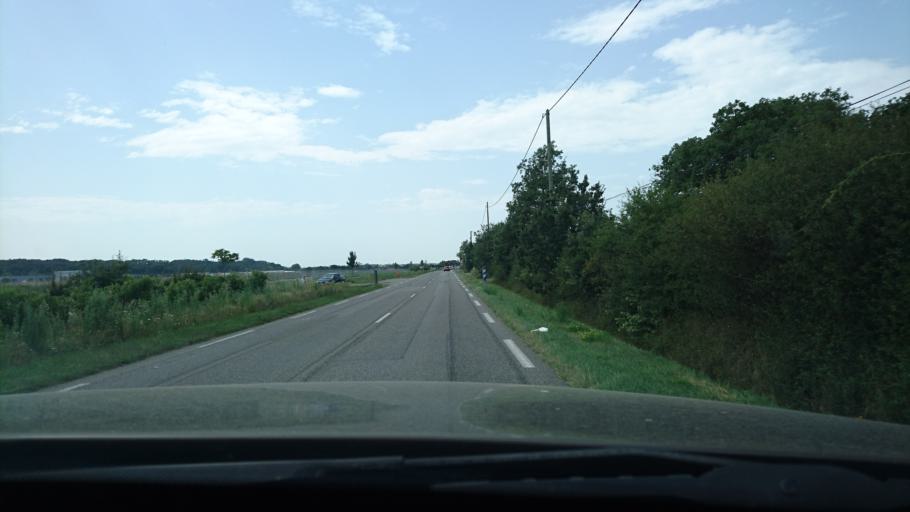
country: FR
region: Midi-Pyrenees
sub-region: Departement de la Haute-Garonne
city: Cornebarrieu
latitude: 43.6473
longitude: 1.3473
